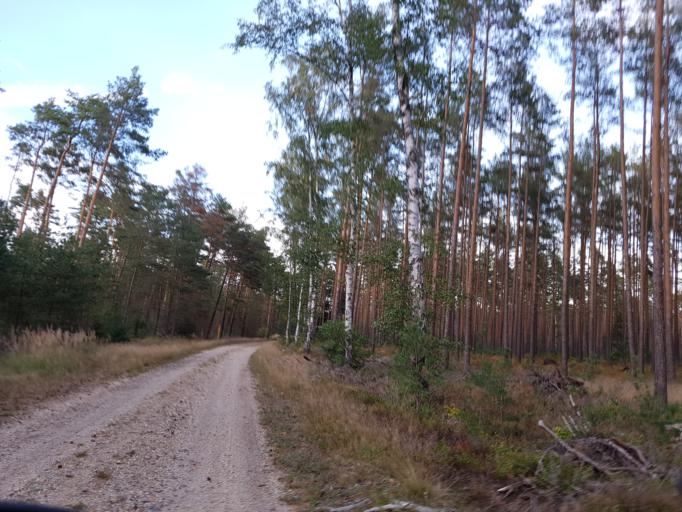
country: DE
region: Brandenburg
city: Trobitz
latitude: 51.5611
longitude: 13.4535
